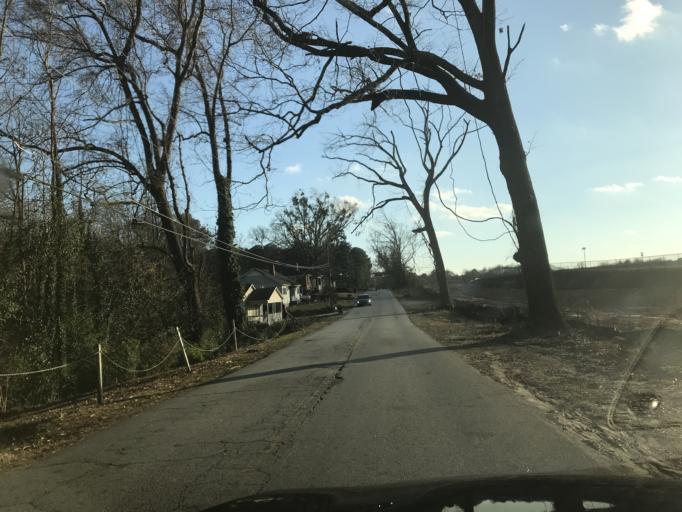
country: US
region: Georgia
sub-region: Fulton County
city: College Park
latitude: 33.6290
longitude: -84.4841
